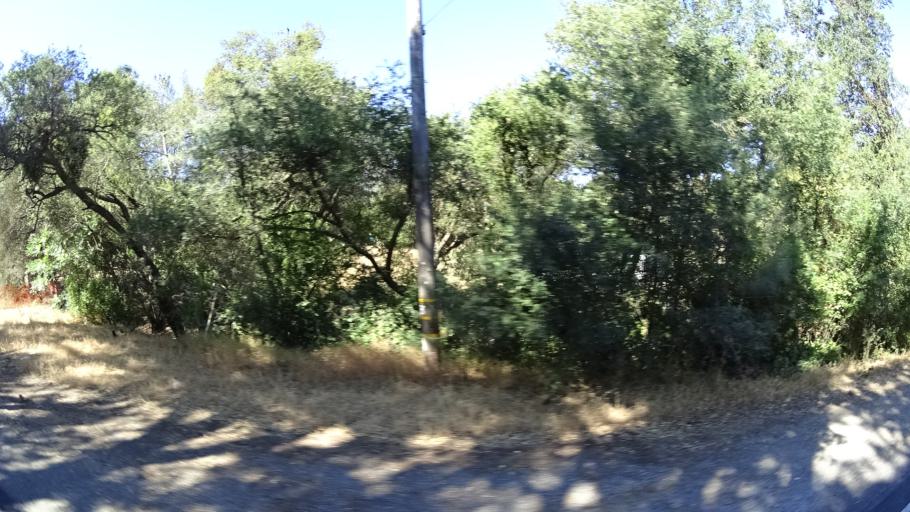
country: US
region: California
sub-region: Calaveras County
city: San Andreas
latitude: 38.2042
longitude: -120.6807
